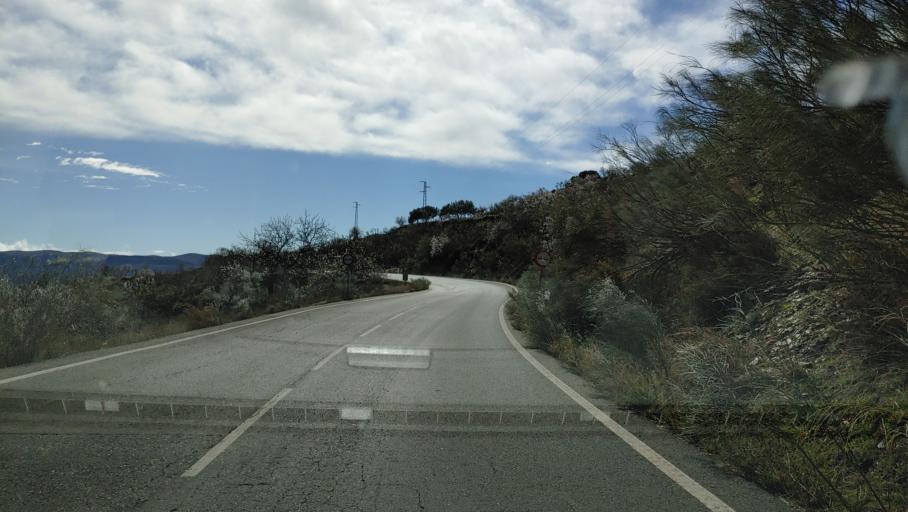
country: ES
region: Andalusia
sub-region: Provincia de Almeria
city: Ohanes
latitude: 37.0455
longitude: -2.7327
